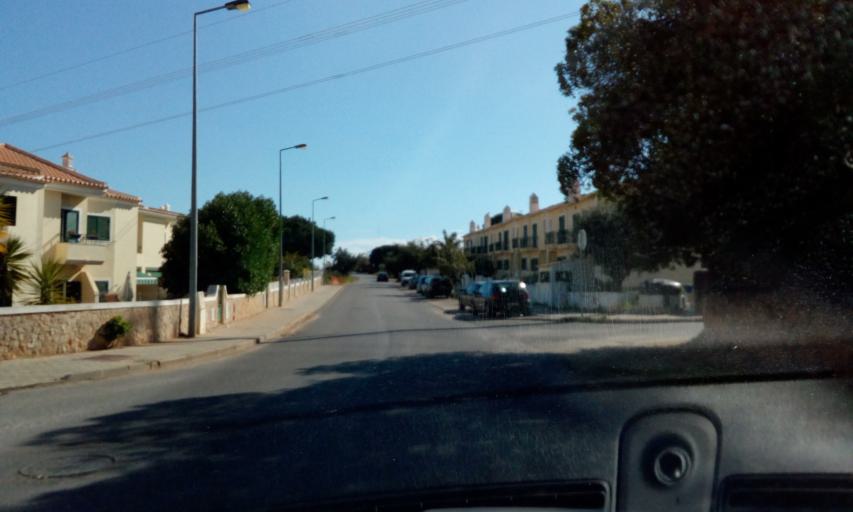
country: PT
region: Faro
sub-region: Albufeira
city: Ferreiras
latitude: 37.1138
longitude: -8.2129
